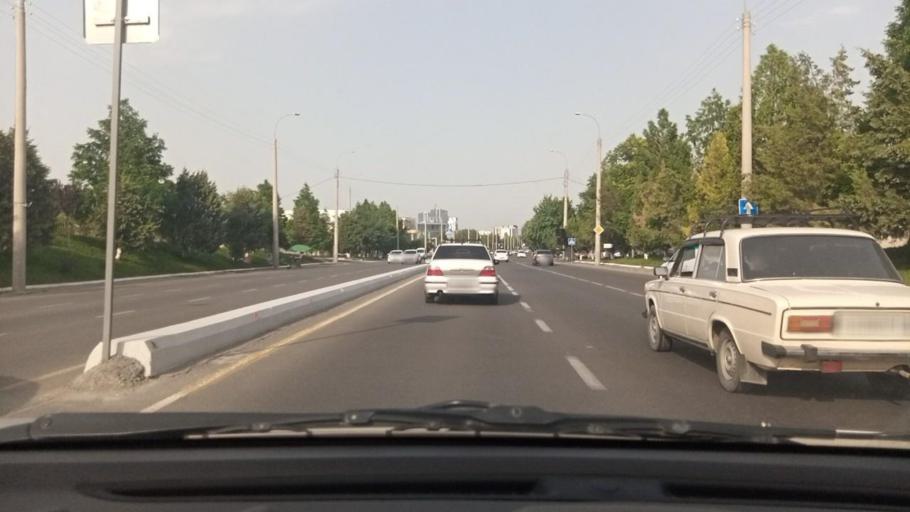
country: UZ
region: Toshkent
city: Salor
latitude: 41.3351
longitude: 69.3132
